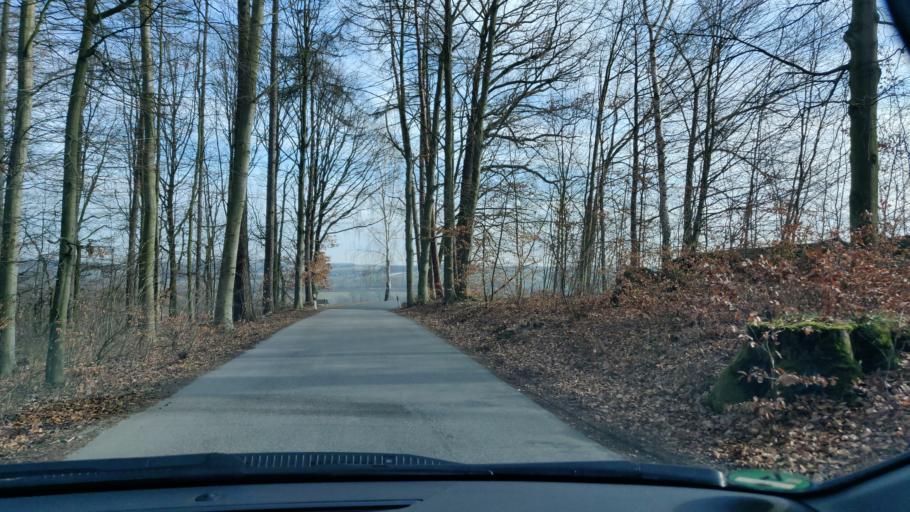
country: DE
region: Saxony
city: Rochlitz
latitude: 51.0308
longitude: 12.7825
